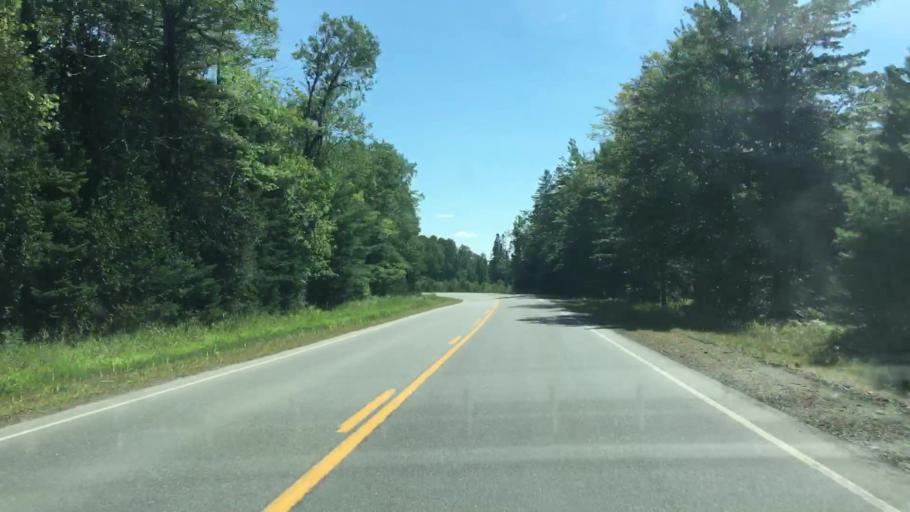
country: US
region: Maine
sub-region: Piscataquis County
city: Milo
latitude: 45.2013
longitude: -68.9070
